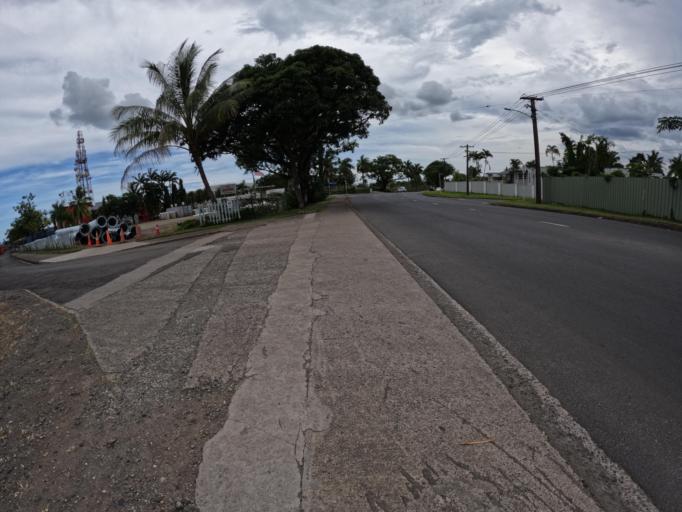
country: FJ
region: Central
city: Suva
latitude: -18.1155
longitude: 178.4384
